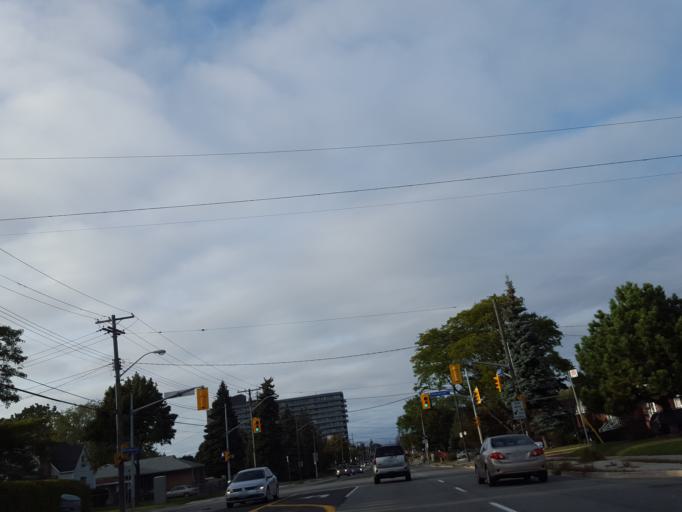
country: CA
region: Ontario
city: Scarborough
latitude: 43.7419
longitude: -79.2933
